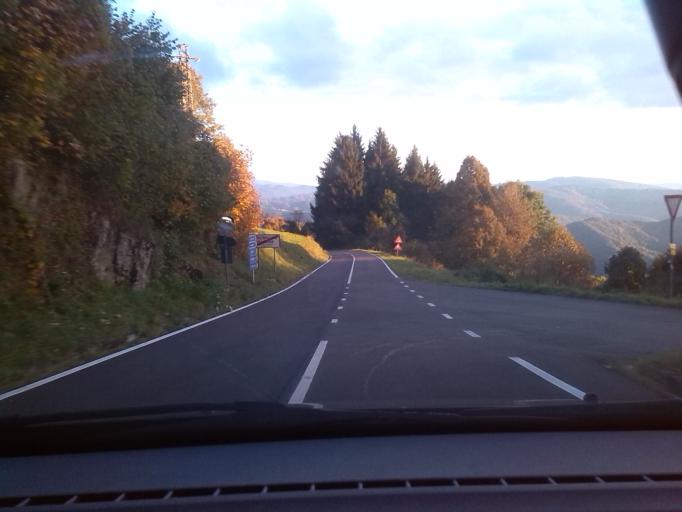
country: IT
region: Friuli Venezia Giulia
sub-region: Provincia di Udine
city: Savogna
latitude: 46.1943
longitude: 13.5335
